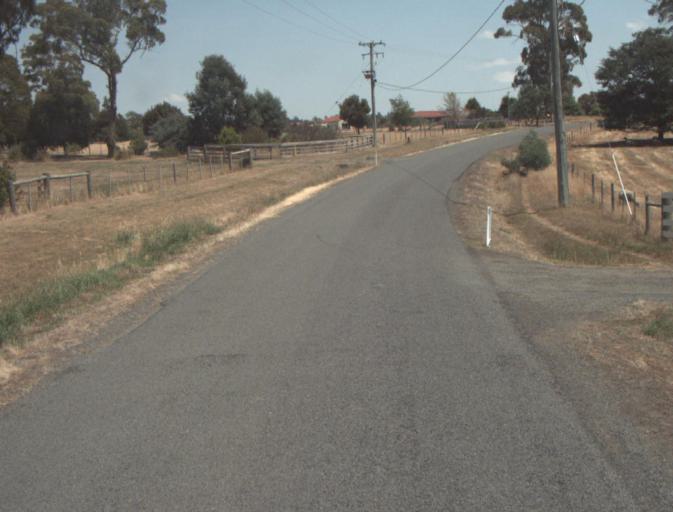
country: AU
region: Tasmania
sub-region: Launceston
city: Newstead
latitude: -41.4999
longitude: 147.2108
